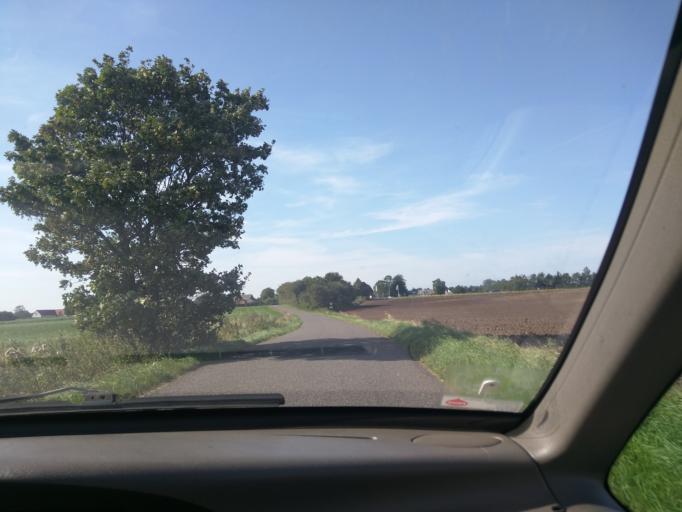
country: DK
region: Central Jutland
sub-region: Viborg Kommune
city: Bjerringbro
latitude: 56.4773
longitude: 9.6073
